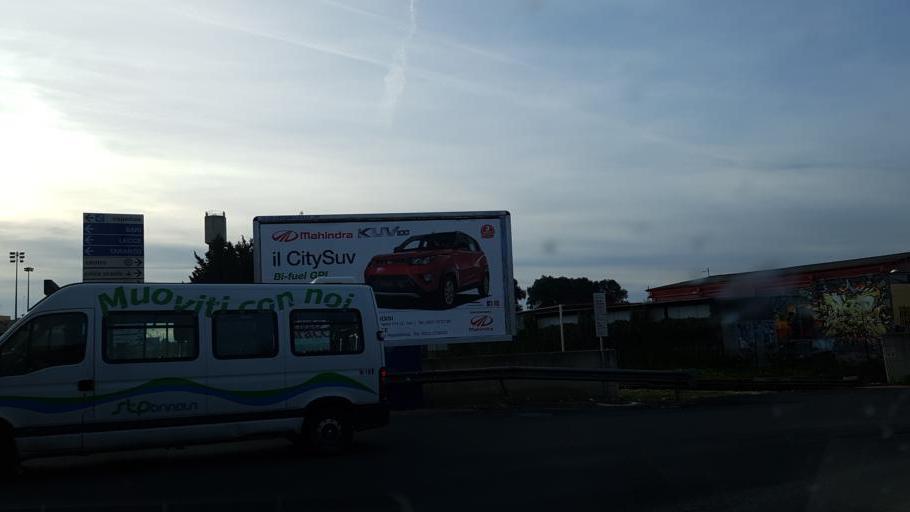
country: IT
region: Apulia
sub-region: Provincia di Brindisi
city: Brindisi
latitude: 40.6286
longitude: 17.9470
